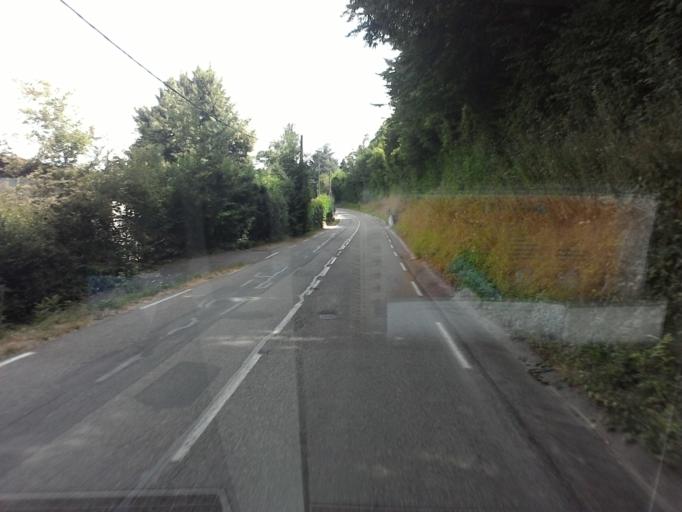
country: FR
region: Rhone-Alpes
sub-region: Departement de l'Isere
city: Bilieu
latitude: 45.4431
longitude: 5.5291
